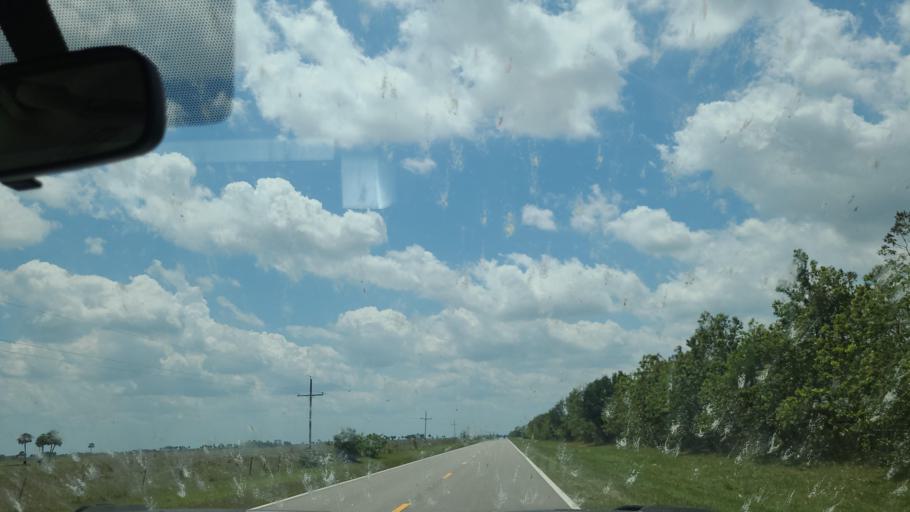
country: US
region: Florida
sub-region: Glades County
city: Buckhead Ridge
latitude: 27.2738
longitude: -81.0536
